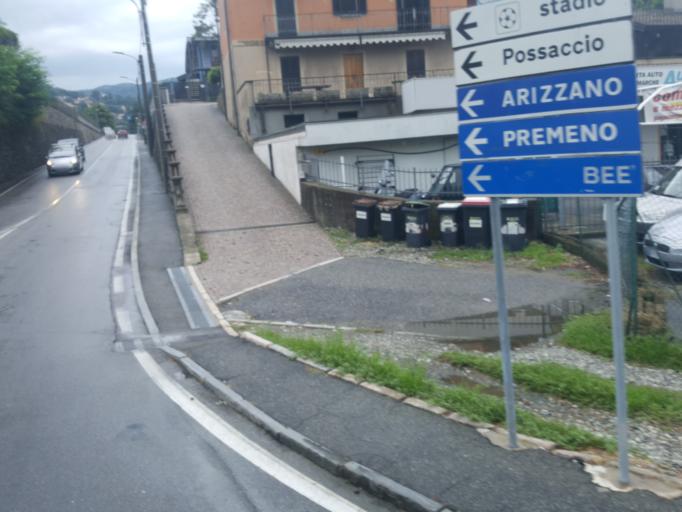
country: IT
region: Piedmont
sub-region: Provincia Verbano-Cusio-Ossola
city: Pallanza-Intra-Suna
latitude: 45.9391
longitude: 8.5578
